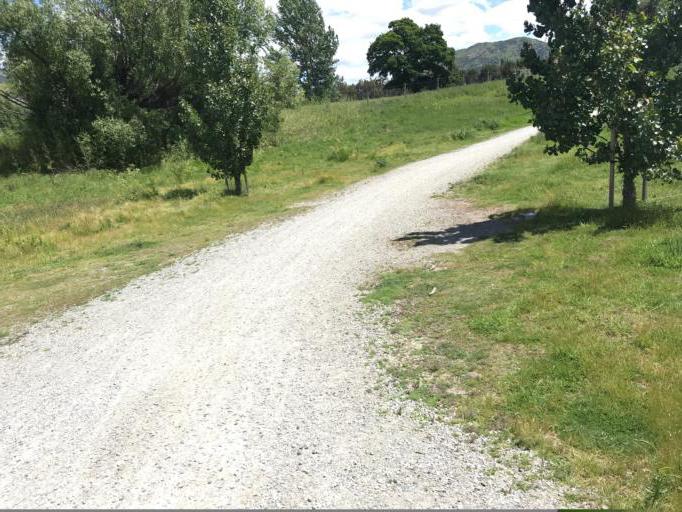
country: NZ
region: Otago
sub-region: Queenstown-Lakes District
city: Arrowtown
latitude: -45.0016
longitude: 168.8732
